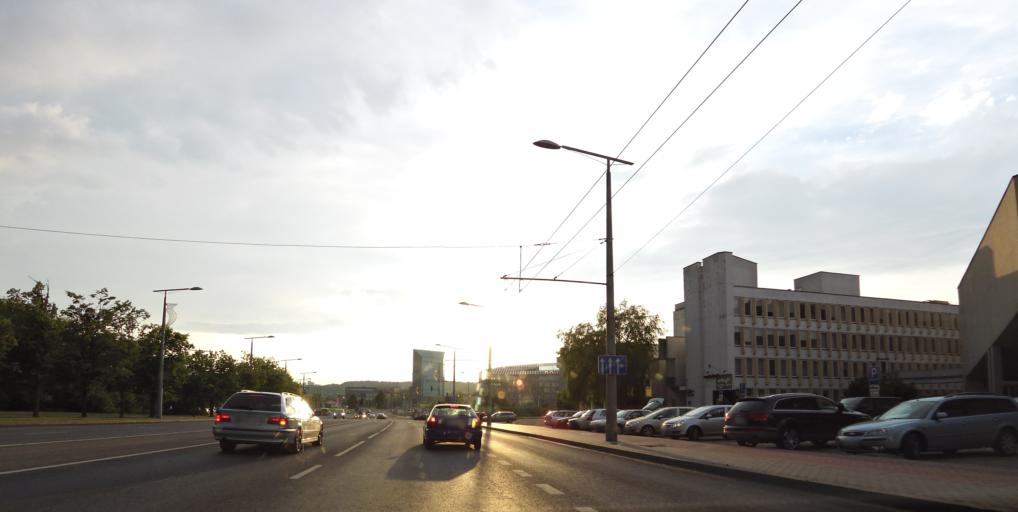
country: LT
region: Vilnius County
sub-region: Vilnius
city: Vilnius
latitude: 54.6980
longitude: 25.2694
